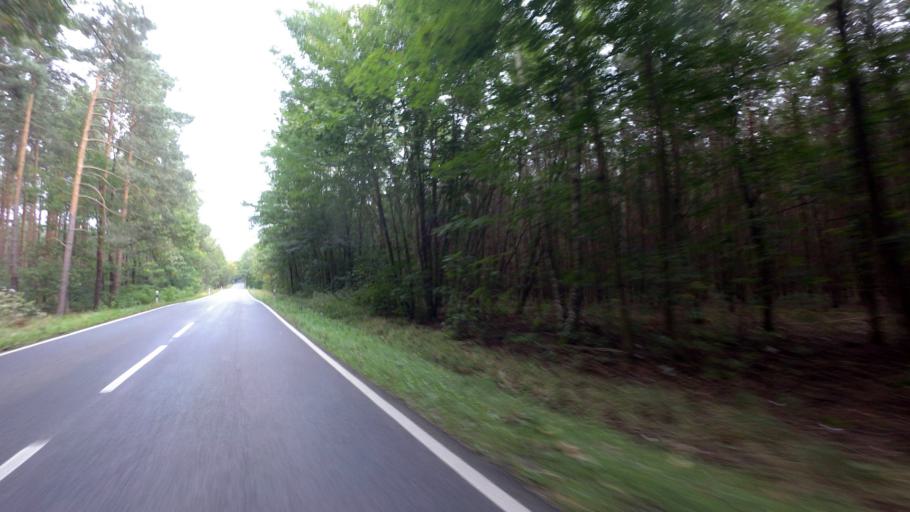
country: DE
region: Brandenburg
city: Baruth
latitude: 52.0326
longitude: 13.4820
